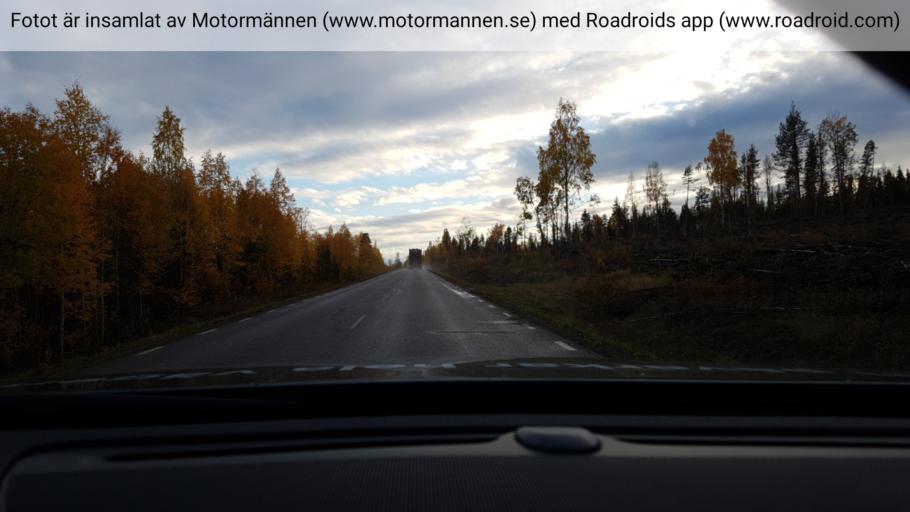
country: SE
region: Norrbotten
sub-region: Overkalix Kommun
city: OEverkalix
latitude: 66.8174
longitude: 22.7451
